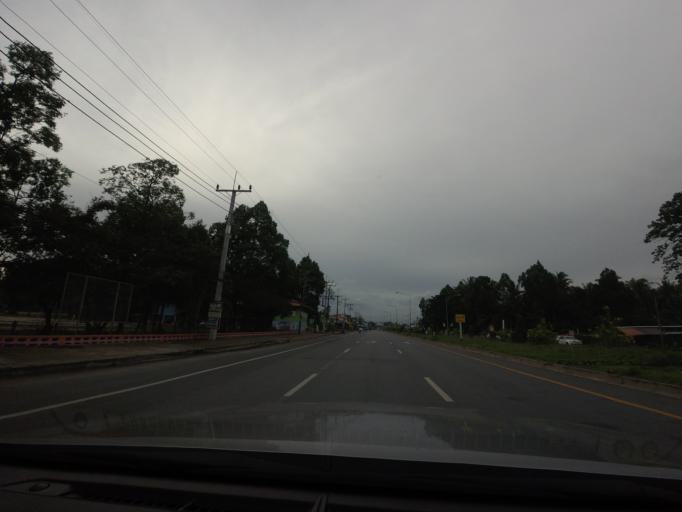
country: TH
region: Nakhon Si Thammarat
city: Chian Yai
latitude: 8.1081
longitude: 100.1012
